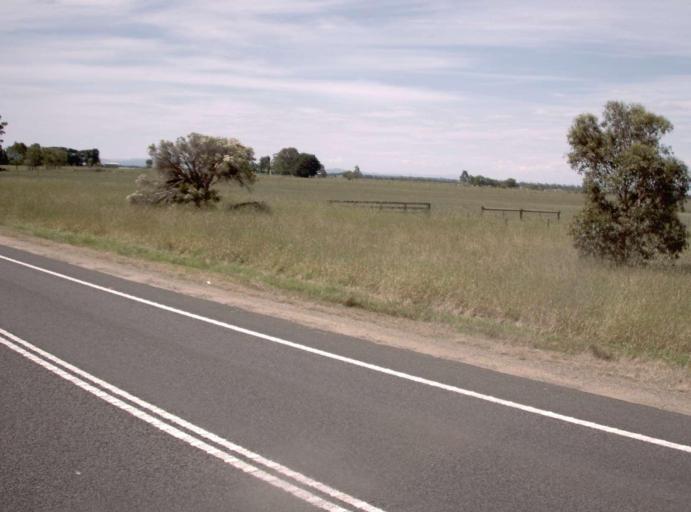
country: AU
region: Victoria
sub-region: Wellington
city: Sale
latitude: -38.0599
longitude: 147.0702
